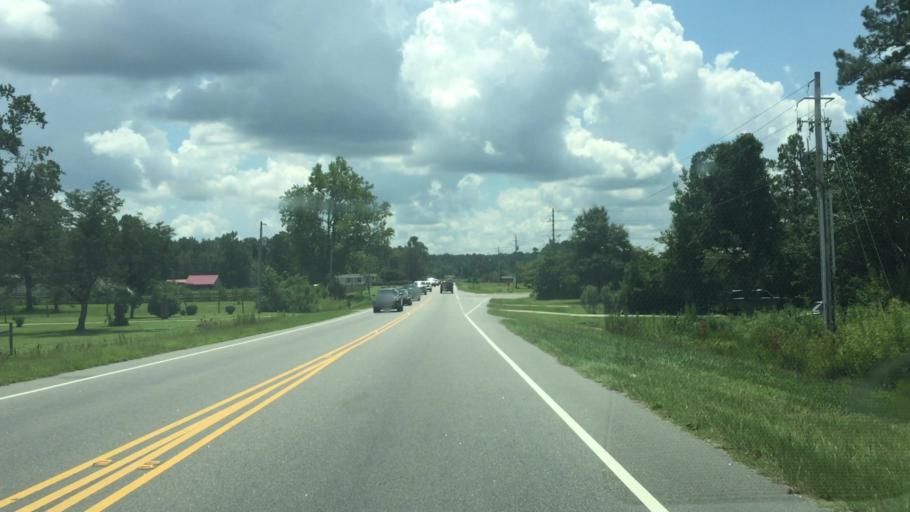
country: US
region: North Carolina
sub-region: Columbus County
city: Chadbourn
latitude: 34.3570
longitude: -78.8297
